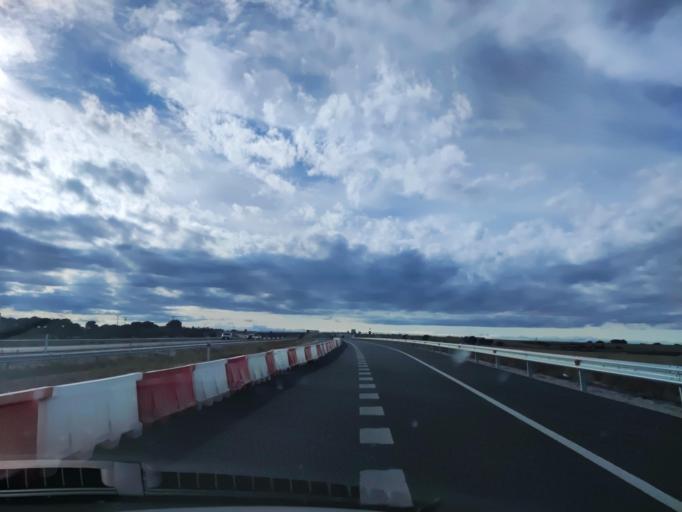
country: ES
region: Castille and Leon
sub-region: Provincia de Salamanca
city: Fuentes de Onoro
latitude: 40.5932
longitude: -6.7901
